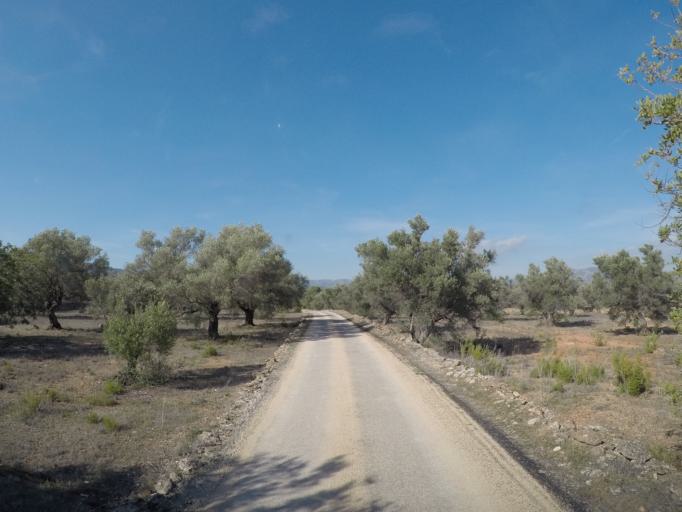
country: ES
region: Catalonia
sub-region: Provincia de Tarragona
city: El Perello
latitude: 40.9059
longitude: 0.7269
